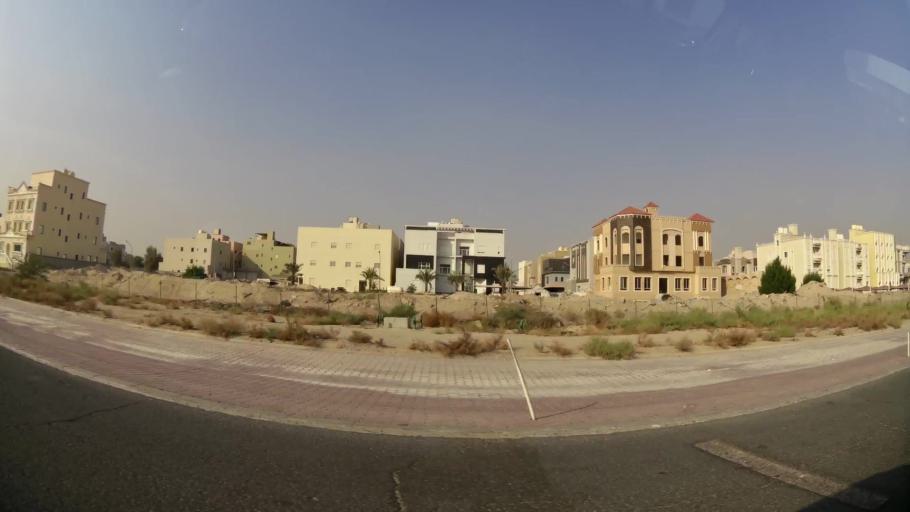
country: KW
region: Mubarak al Kabir
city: Mubarak al Kabir
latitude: 29.1931
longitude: 48.1089
